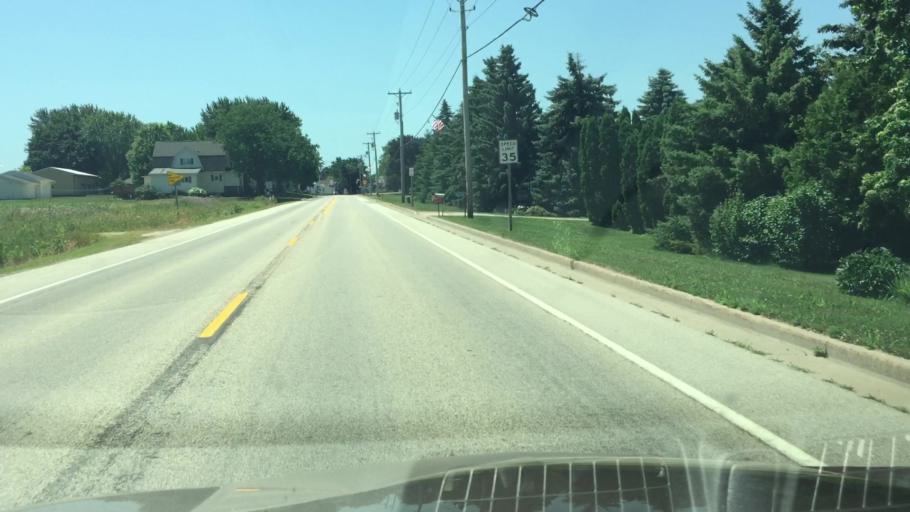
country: US
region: Wisconsin
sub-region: Fond du Lac County
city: Saint Peter
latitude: 43.9172
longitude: -88.3114
